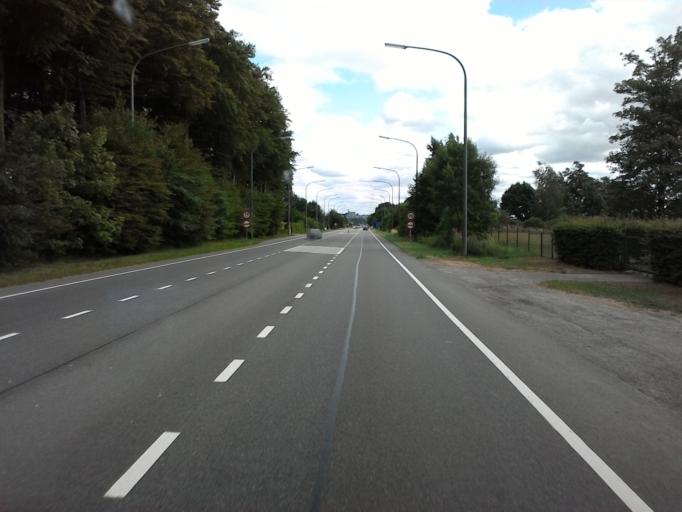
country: BE
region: Wallonia
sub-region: Province du Luxembourg
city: Arlon
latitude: 49.7109
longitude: 5.8023
